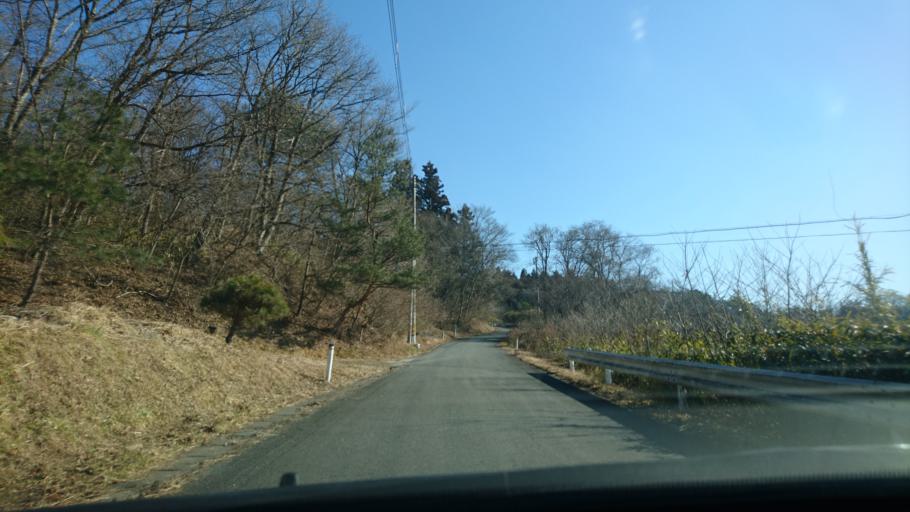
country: JP
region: Iwate
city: Ichinoseki
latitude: 38.8493
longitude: 141.2328
